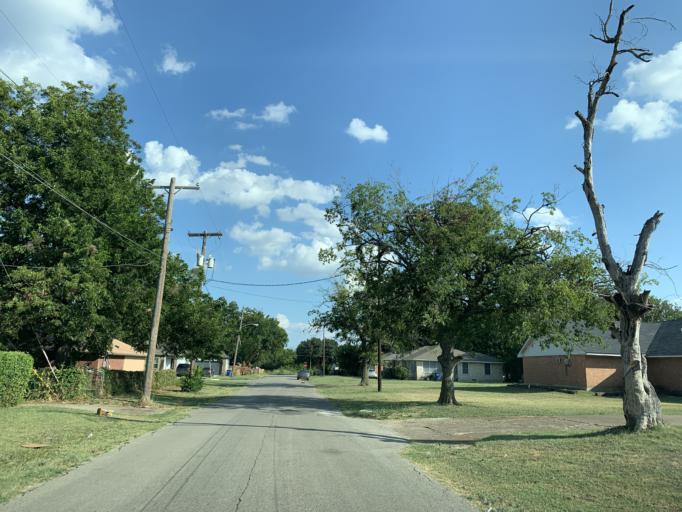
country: US
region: Texas
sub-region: Dallas County
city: Hutchins
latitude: 32.6991
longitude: -96.7788
